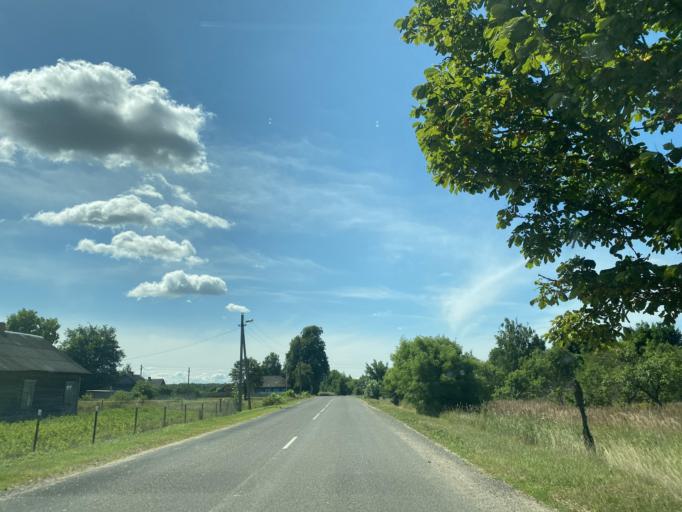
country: BY
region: Brest
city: Ivanava
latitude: 52.2083
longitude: 25.6288
